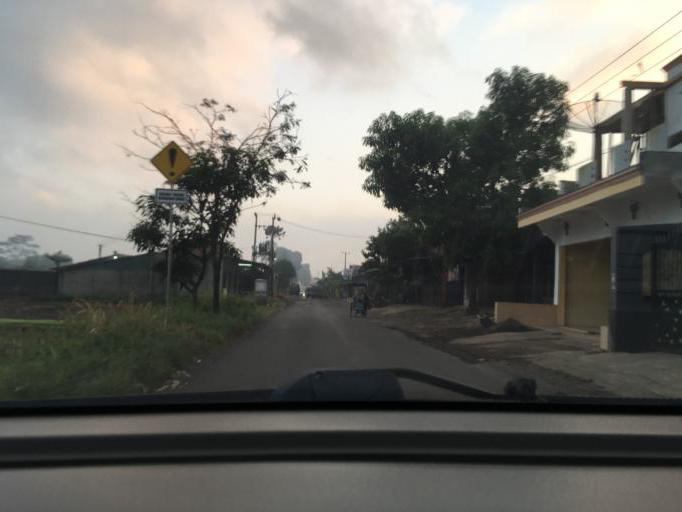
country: ID
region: West Java
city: Padamulya
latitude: -7.2095
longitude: 108.1997
